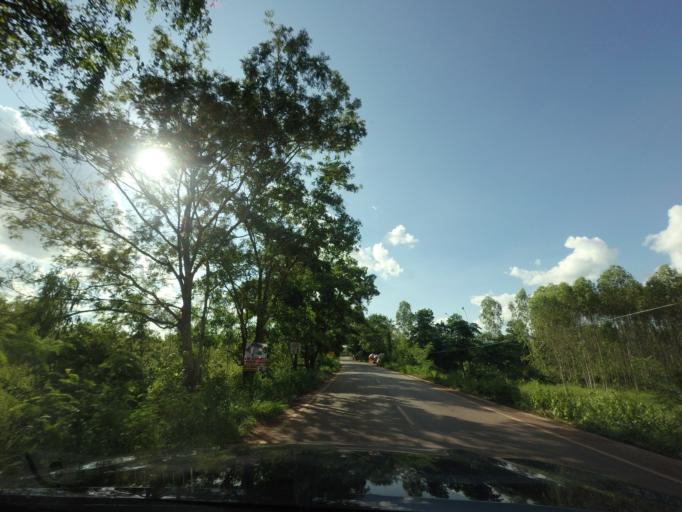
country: TH
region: Changwat Udon Thani
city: Ban Dung
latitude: 17.7437
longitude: 103.3382
